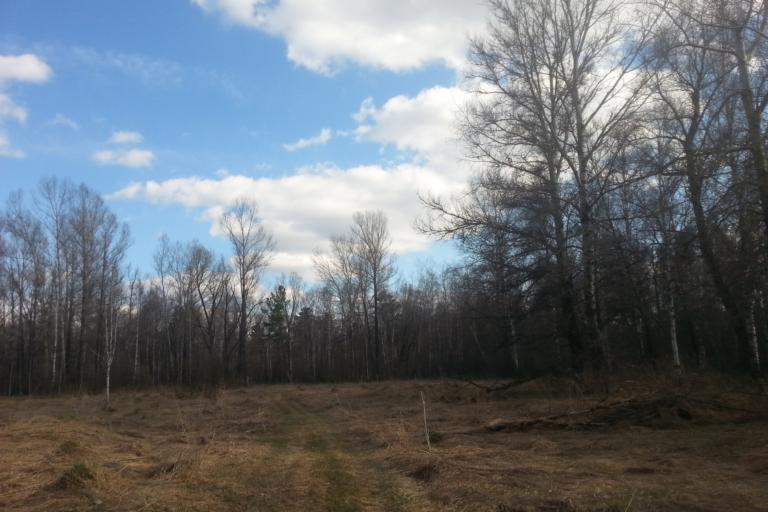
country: RU
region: Altai Krai
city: Sannikovo
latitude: 53.3322
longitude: 84.0201
